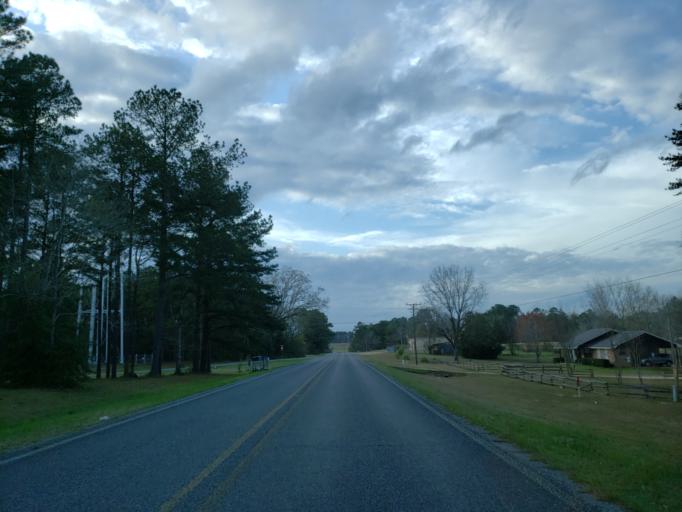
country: US
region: Mississippi
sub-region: Clarke County
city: Stonewall
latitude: 32.2068
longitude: -88.6914
